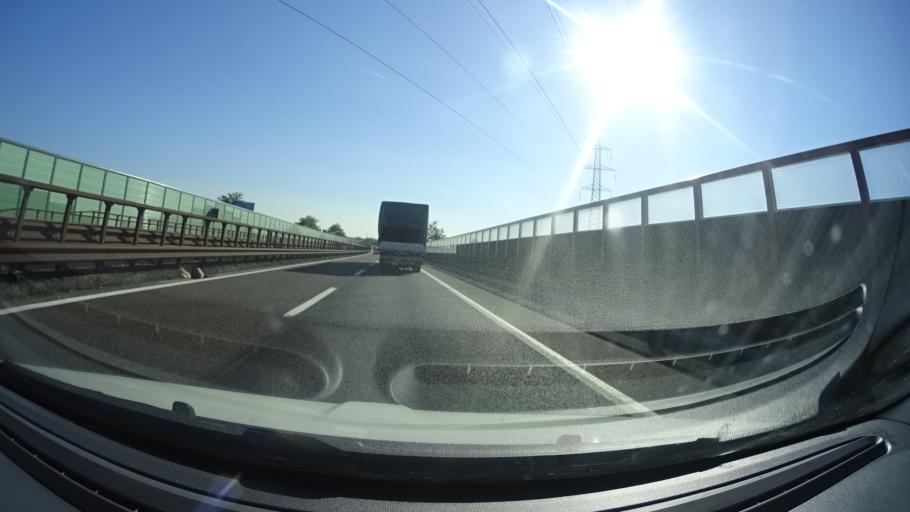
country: IT
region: Veneto
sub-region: Provincia di Verona
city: Bussolengo
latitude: 45.4581
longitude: 10.8420
